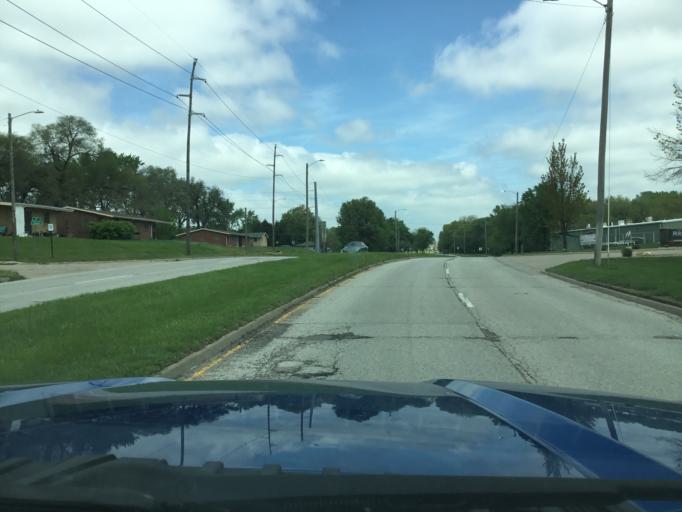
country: US
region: Kansas
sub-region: Shawnee County
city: Topeka
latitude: 39.0353
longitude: -95.6372
